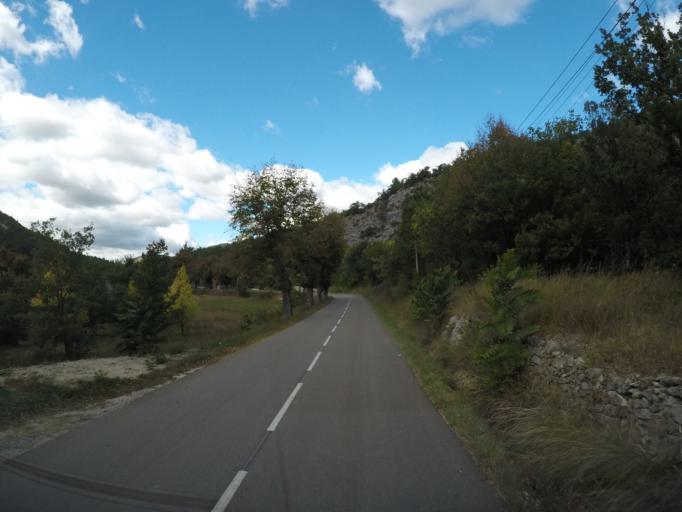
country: FR
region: Provence-Alpes-Cote d'Azur
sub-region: Departement du Vaucluse
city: Sault
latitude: 44.1739
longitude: 5.4056
